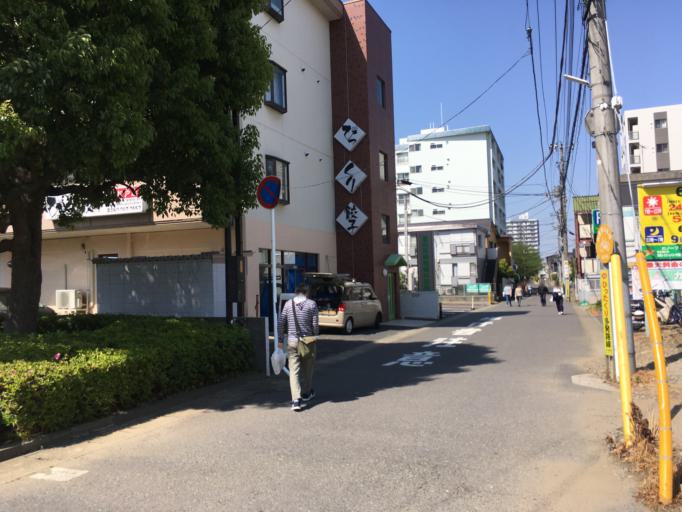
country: JP
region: Chiba
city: Matsudo
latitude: 35.8019
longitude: 139.9121
